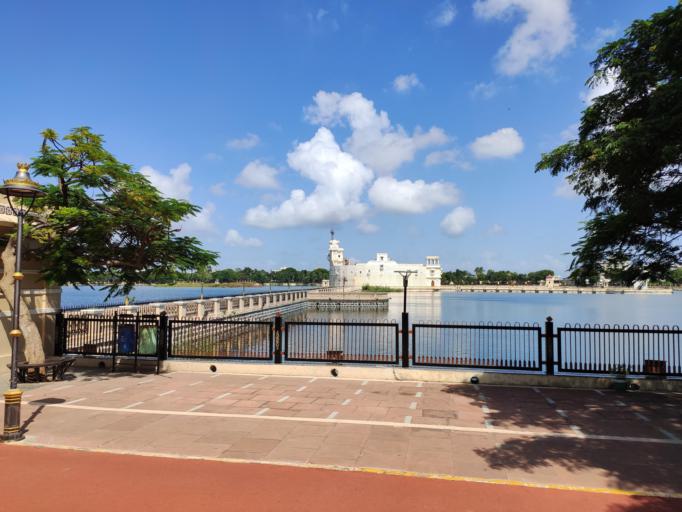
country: IN
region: Gujarat
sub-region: Jamnagar
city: Jamnagar
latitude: 22.4626
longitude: 70.0703
